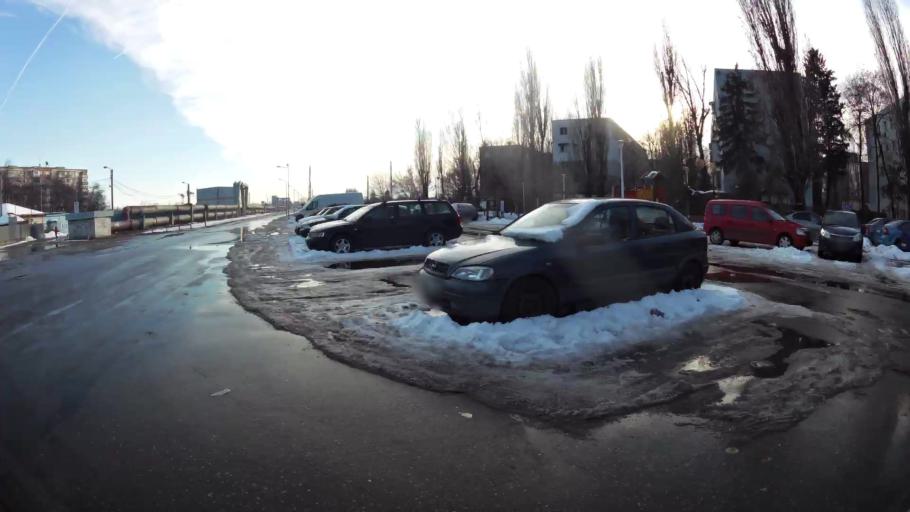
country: RO
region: Bucuresti
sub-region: Municipiul Bucuresti
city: Bucuresti
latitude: 44.3859
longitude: 26.0865
